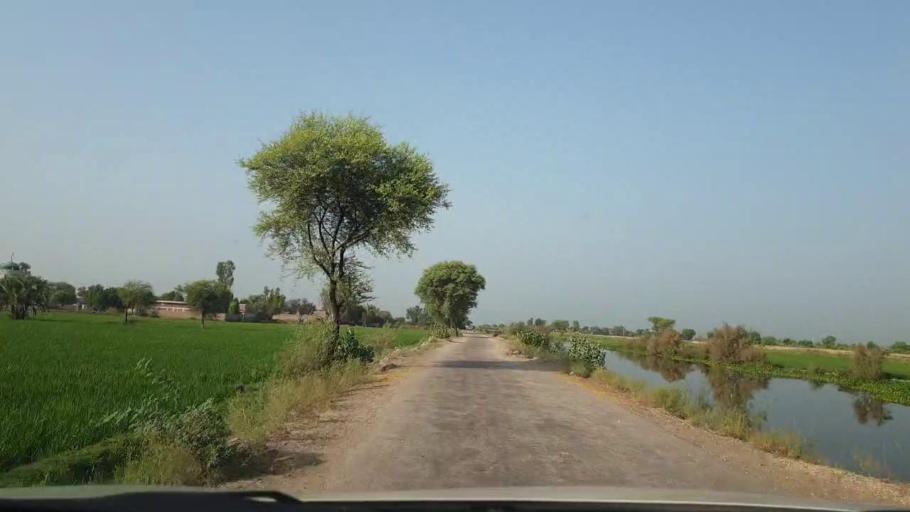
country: PK
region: Sindh
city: Larkana
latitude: 27.5071
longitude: 68.1806
